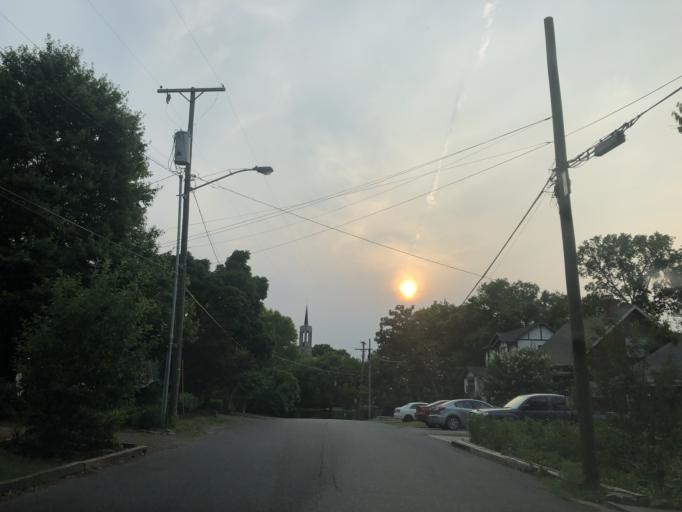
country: US
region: Tennessee
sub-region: Davidson County
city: Oak Hill
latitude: 36.1185
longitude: -86.7946
